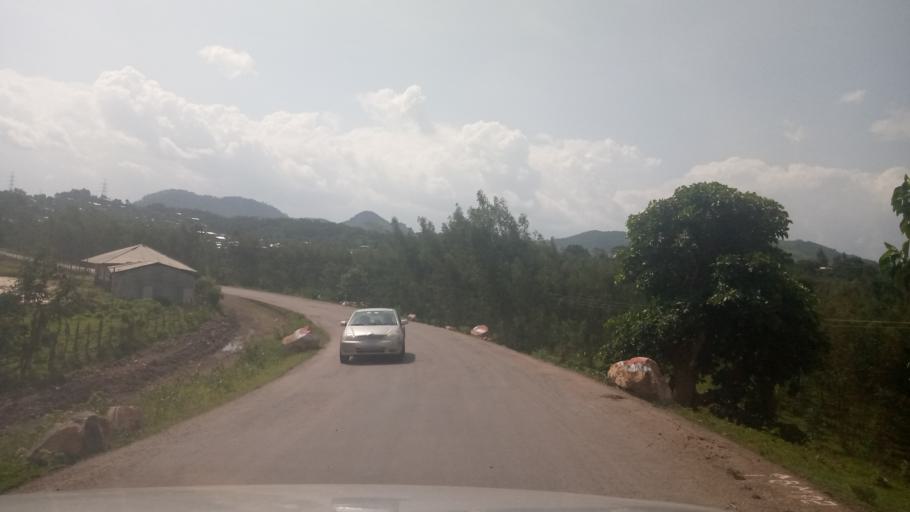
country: ET
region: Oromiya
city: Agaro
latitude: 7.9949
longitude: 36.5042
